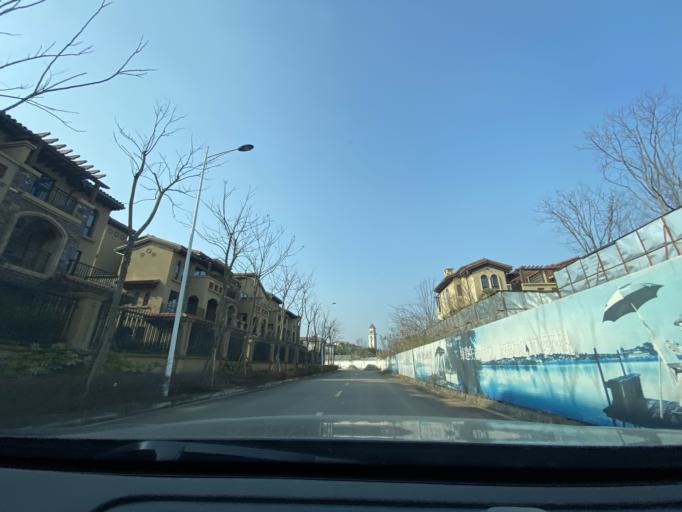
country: CN
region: Sichuan
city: Wenlin
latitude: 30.2539
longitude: 104.2452
